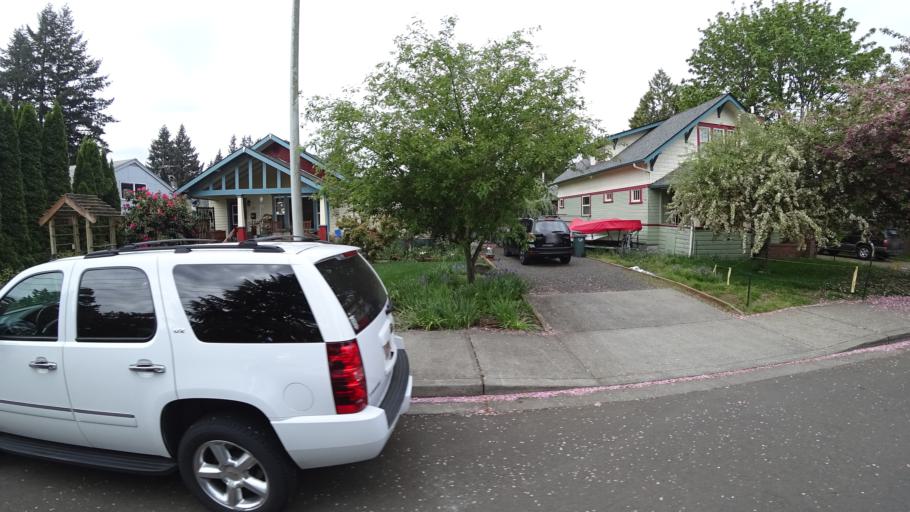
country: US
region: Oregon
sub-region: Washington County
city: Hillsboro
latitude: 45.5243
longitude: -122.9929
